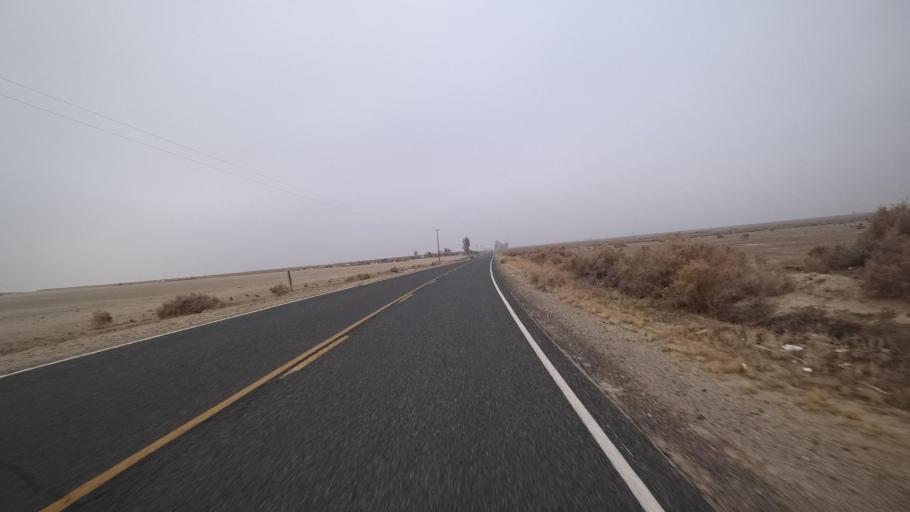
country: US
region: California
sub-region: Kern County
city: Buttonwillow
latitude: 35.3560
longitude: -119.4741
